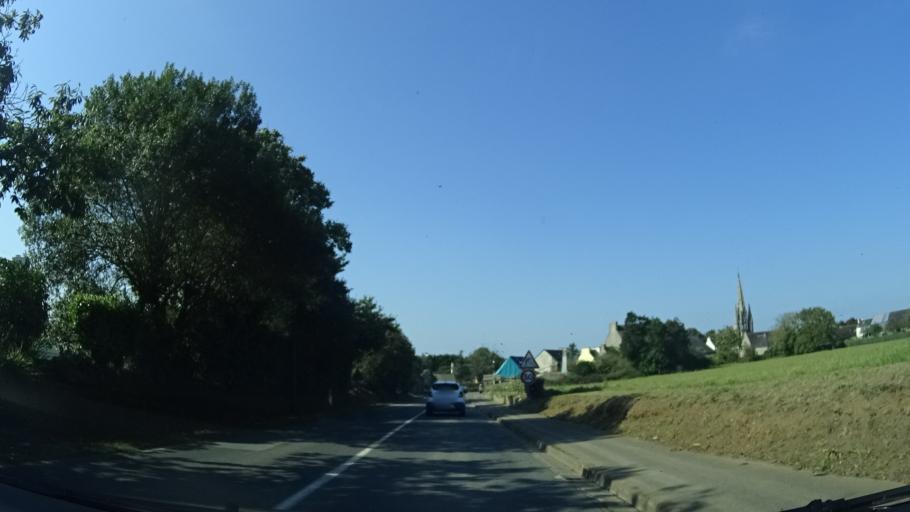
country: FR
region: Brittany
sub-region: Departement du Finistere
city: Plonevez-Porzay
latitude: 48.0909
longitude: -4.2701
